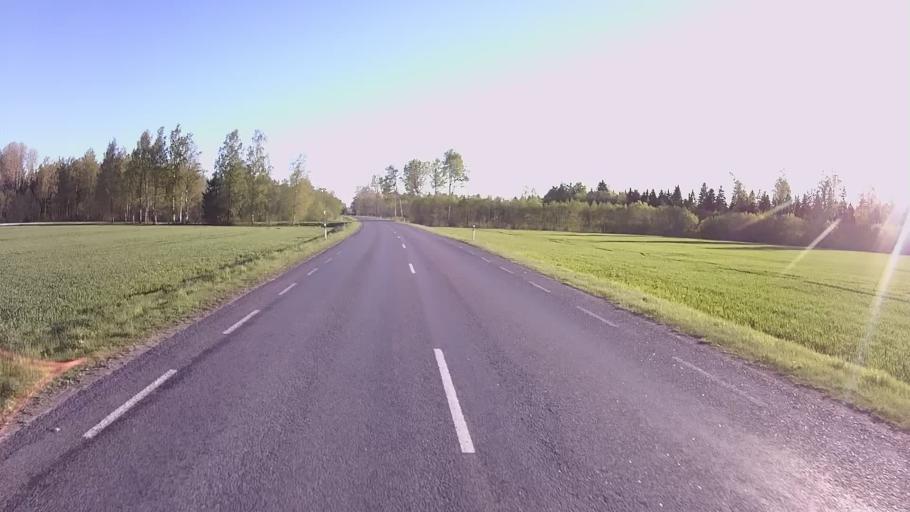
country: EE
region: Viljandimaa
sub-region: Viiratsi vald
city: Viiratsi
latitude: 58.4337
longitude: 25.7230
